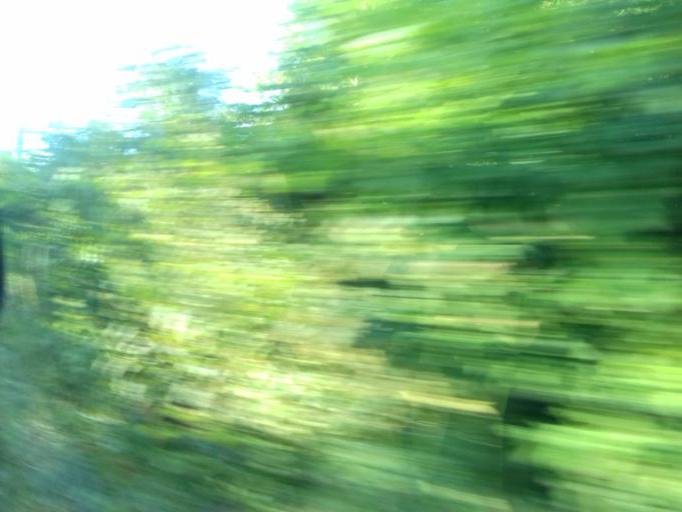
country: IE
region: Leinster
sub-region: An Mhi
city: Ashbourne
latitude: 53.4700
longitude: -6.3414
